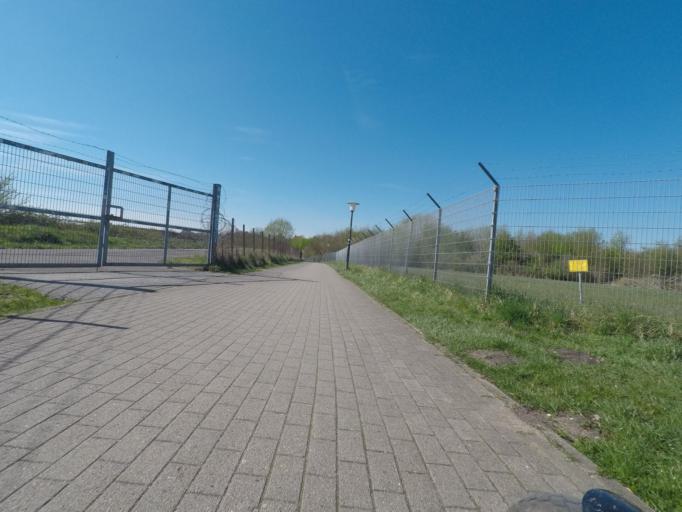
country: DE
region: Hamburg
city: Fuhlsbuettel
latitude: 53.6400
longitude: 10.0078
